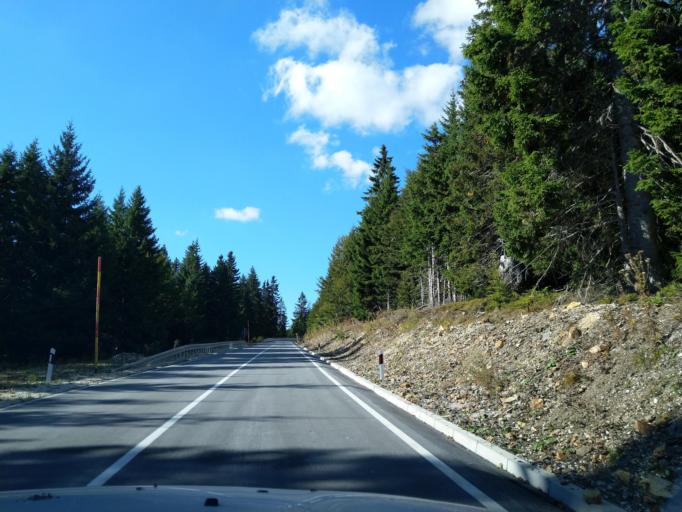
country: RS
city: Sokolovica
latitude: 43.3030
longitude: 20.3062
